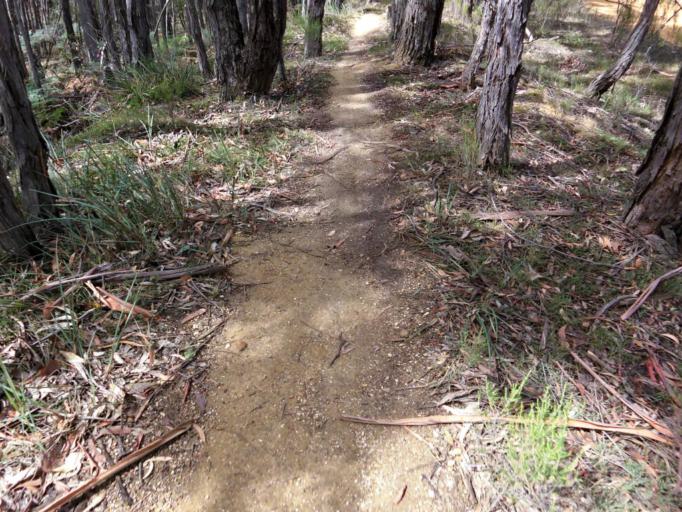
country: AU
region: Victoria
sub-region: Melton
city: Melton West
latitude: -37.4856
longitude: 144.5428
